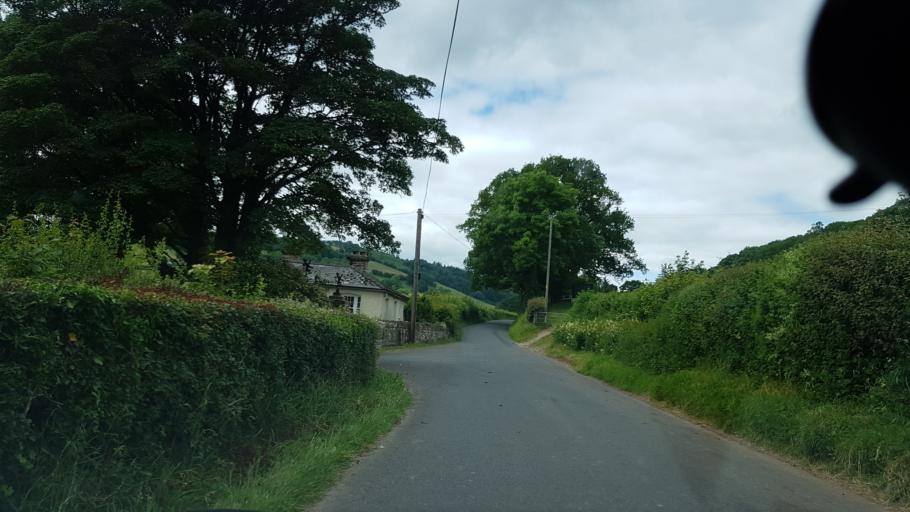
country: GB
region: Wales
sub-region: Monmouthshire
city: Grosmont
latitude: 51.8861
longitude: -2.8209
